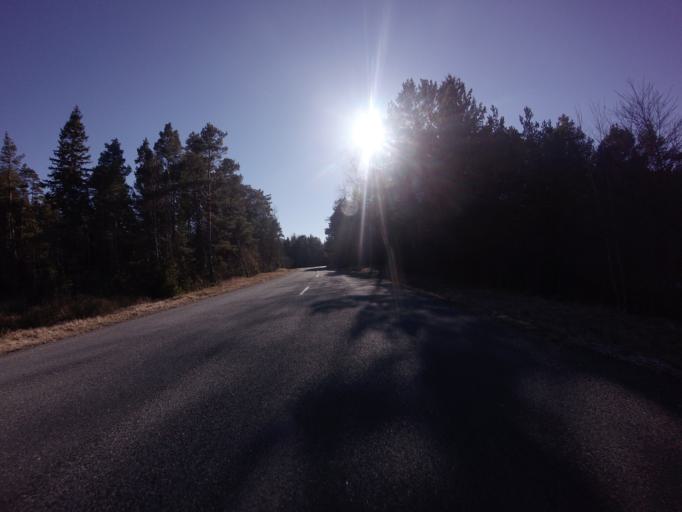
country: EE
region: Saare
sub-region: Kuressaare linn
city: Kuressaare
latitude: 58.5057
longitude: 22.3122
